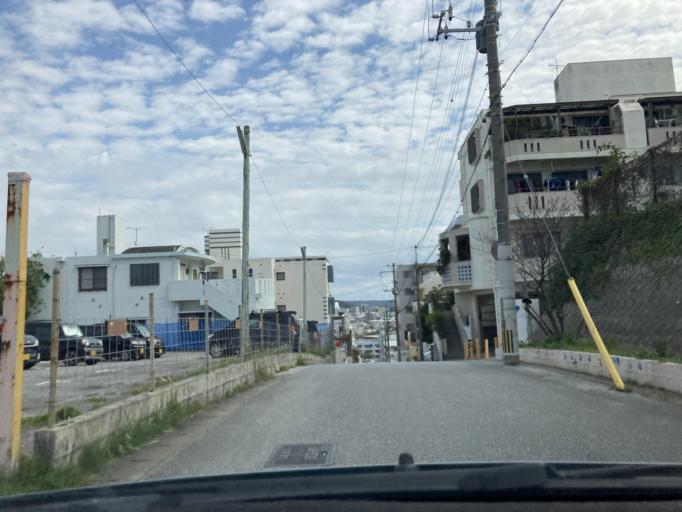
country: JP
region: Okinawa
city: Tomigusuku
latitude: 26.1981
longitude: 127.6937
